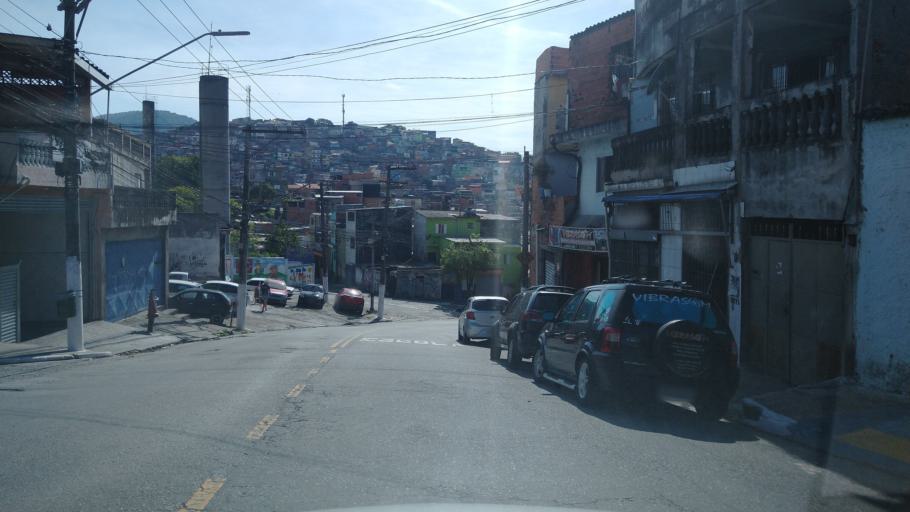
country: BR
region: Sao Paulo
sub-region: Sao Paulo
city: Sao Paulo
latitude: -23.4613
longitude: -46.6792
